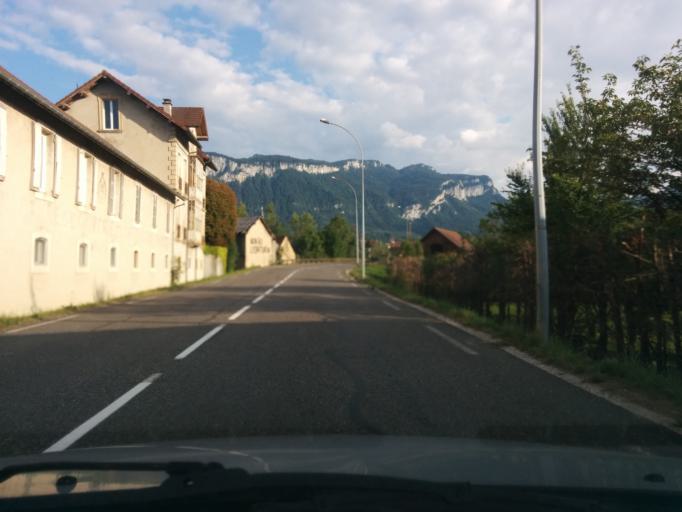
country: FR
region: Rhone-Alpes
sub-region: Departement de la Savoie
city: Les Echelles
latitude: 45.4360
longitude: 5.7521
